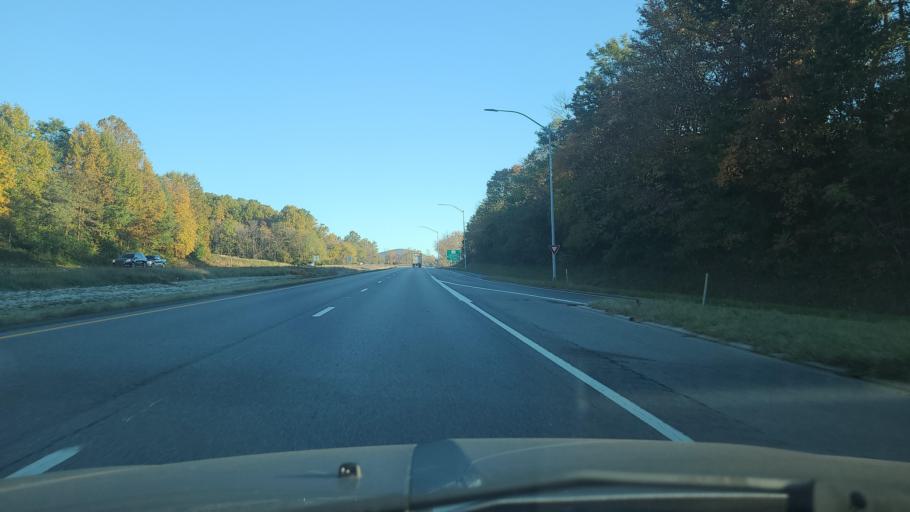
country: US
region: Maryland
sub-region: Frederick County
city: Thurmont
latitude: 39.6271
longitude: -77.4177
